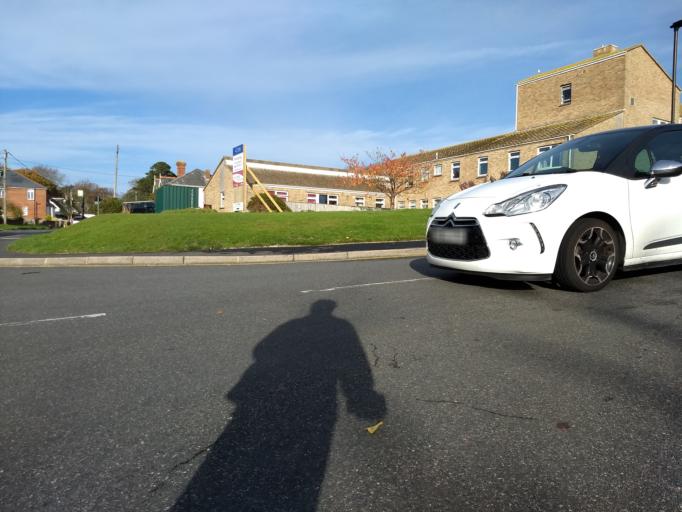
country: GB
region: England
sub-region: Isle of Wight
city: Totland
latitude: 50.6864
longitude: -1.5271
